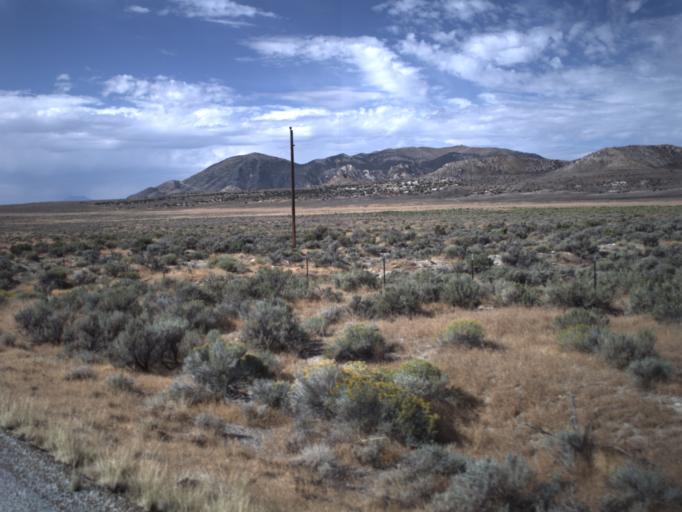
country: US
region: Utah
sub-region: Tooele County
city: Wendover
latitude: 41.5412
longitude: -113.5901
